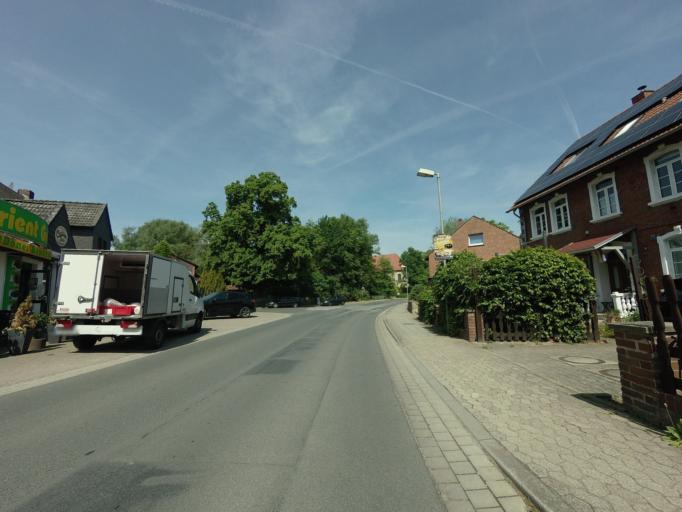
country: DE
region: Lower Saxony
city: Klein Schwulper
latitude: 52.3513
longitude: 10.4354
